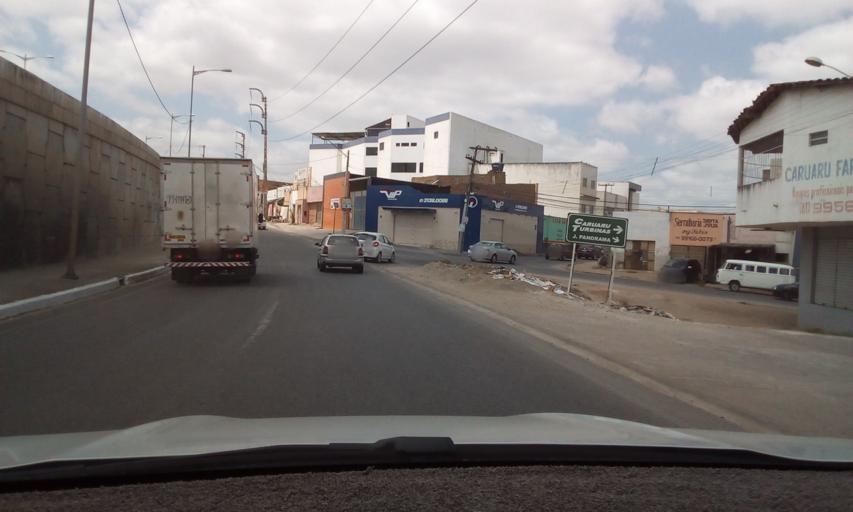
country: BR
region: Pernambuco
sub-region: Caruaru
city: Caruaru
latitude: -8.2730
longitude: -35.9824
